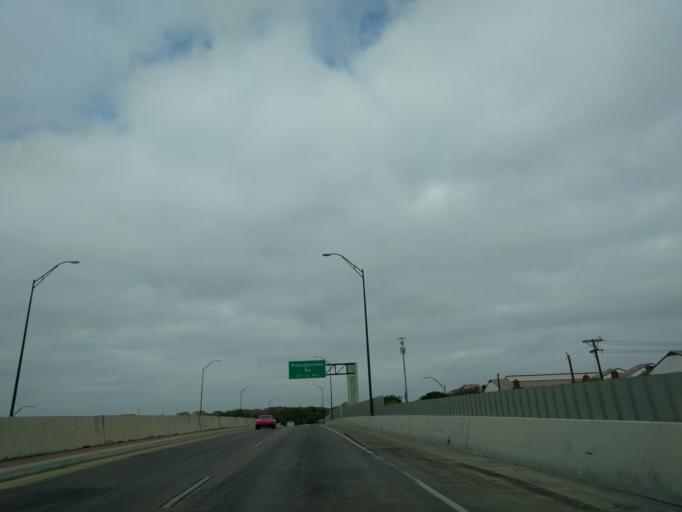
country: US
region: Texas
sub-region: Bexar County
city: Windcrest
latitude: 29.5358
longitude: -98.4107
